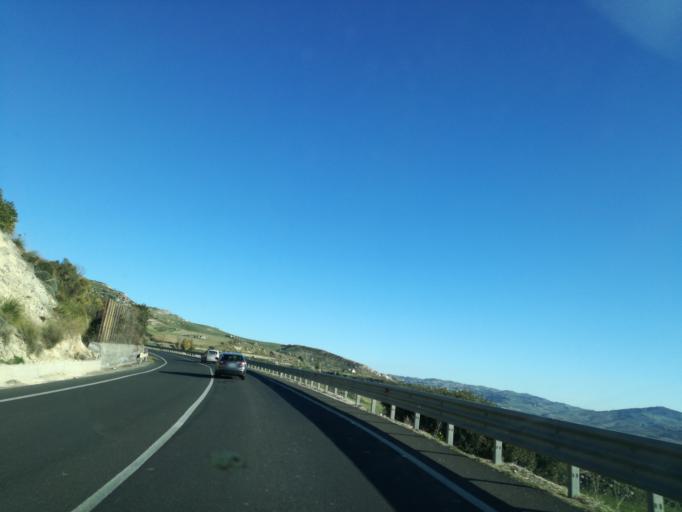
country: IT
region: Sicily
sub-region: Catania
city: San Michele di Ganzaria
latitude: 37.2190
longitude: 14.4263
